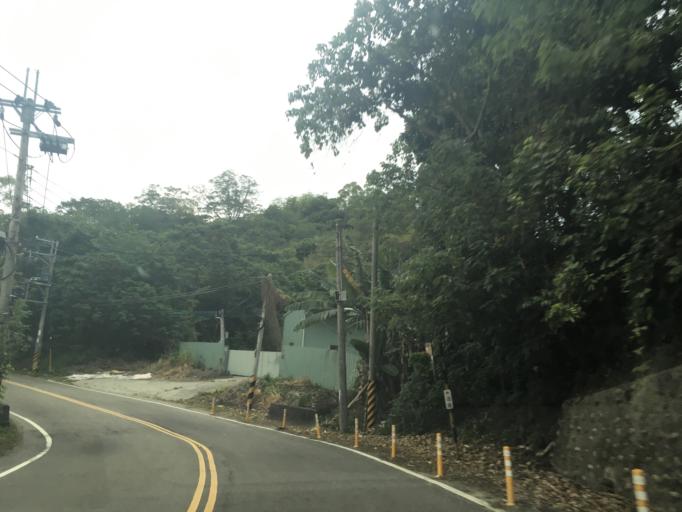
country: TW
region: Taiwan
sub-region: Taichung City
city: Taichung
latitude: 24.1600
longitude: 120.7434
